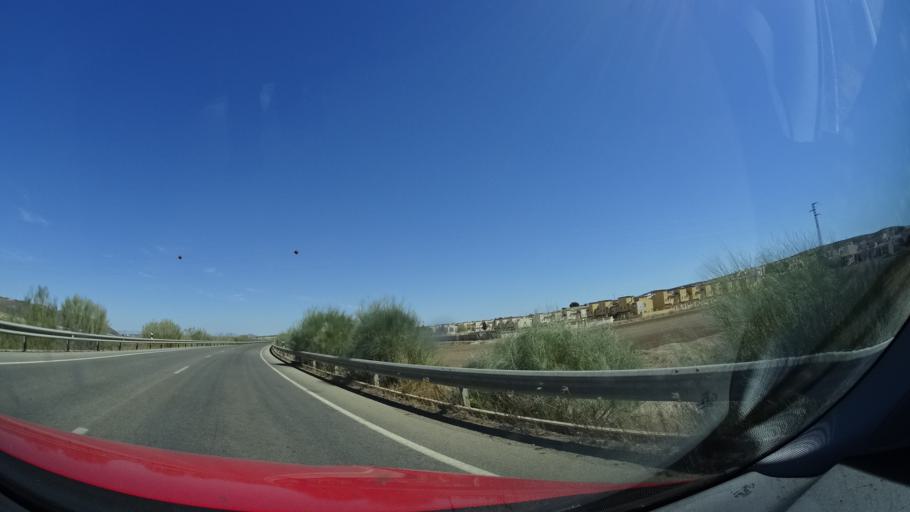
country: ES
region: Andalusia
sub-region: Provincia de Malaga
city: Sierra de Yeguas
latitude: 37.1286
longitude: -4.8745
